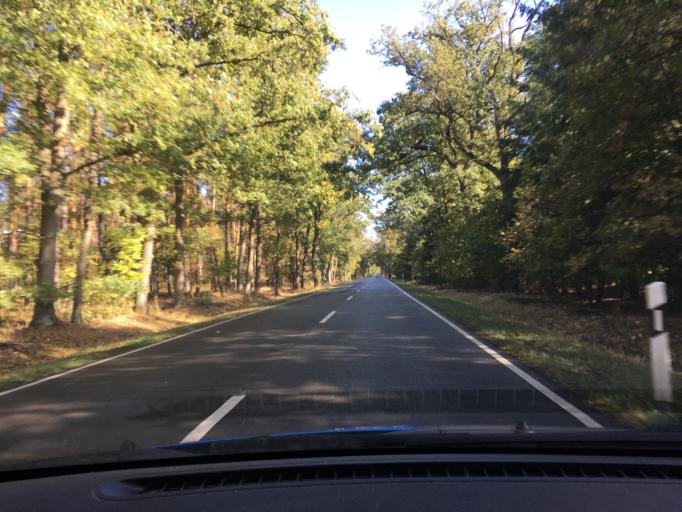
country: DE
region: Saxony-Anhalt
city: Seehausen
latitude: 52.8911
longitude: 11.6956
